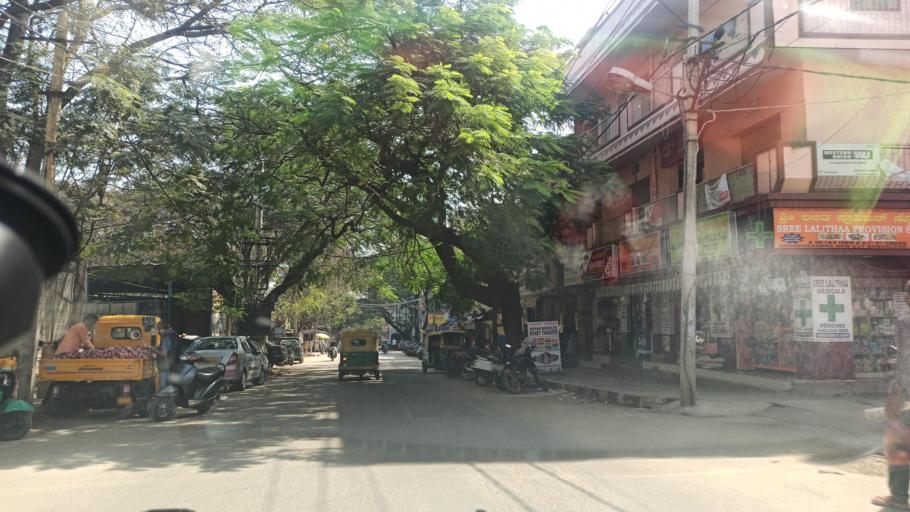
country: IN
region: Karnataka
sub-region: Bangalore Urban
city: Yelahanka
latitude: 13.0426
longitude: 77.5786
